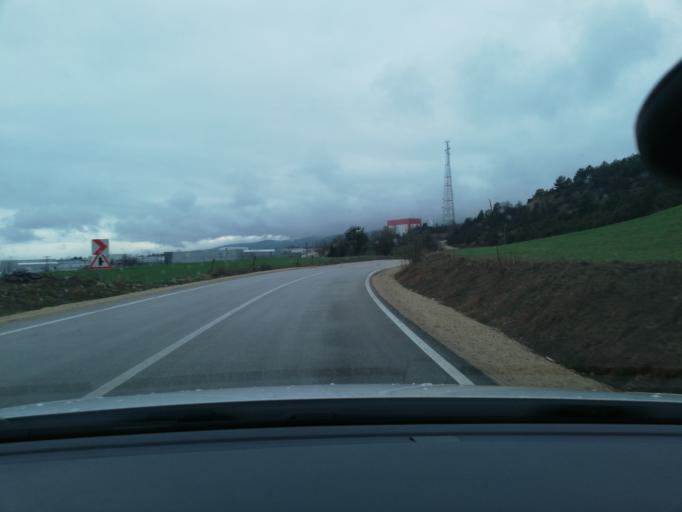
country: TR
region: Bolu
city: Bolu
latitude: 40.7639
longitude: 31.6564
